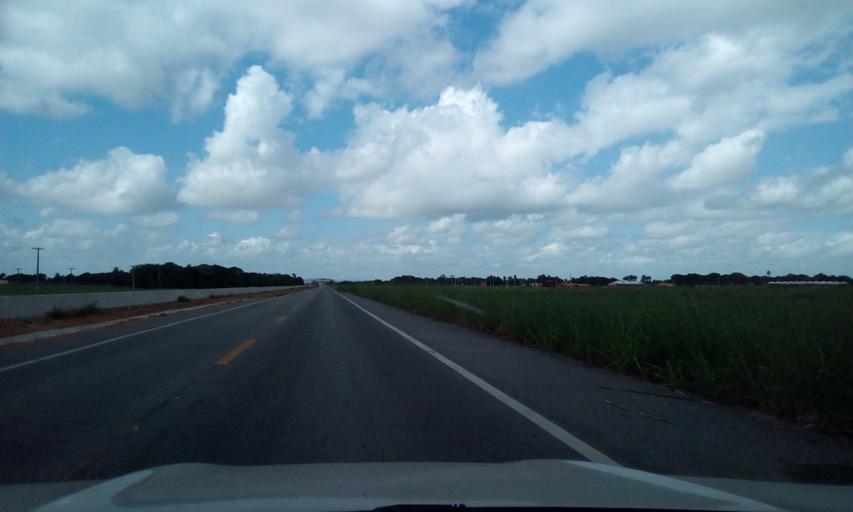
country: BR
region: Alagoas
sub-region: Pilar
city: Pilar
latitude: -9.5789
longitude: -35.9727
